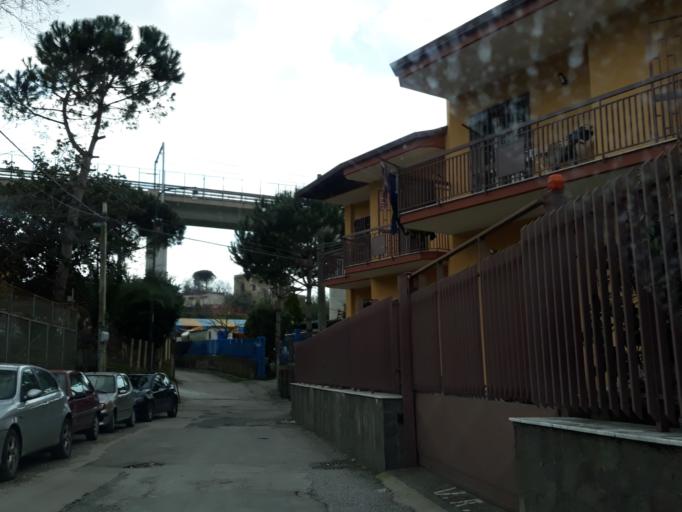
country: IT
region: Campania
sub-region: Provincia di Napoli
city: Napoli
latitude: 40.8824
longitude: 14.2308
